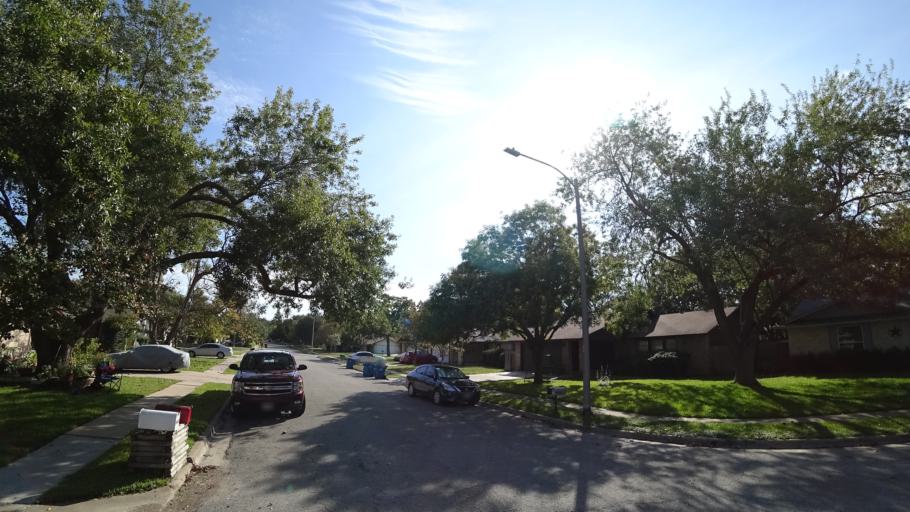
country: US
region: Texas
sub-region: Williamson County
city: Anderson Mill
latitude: 30.4567
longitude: -97.7998
